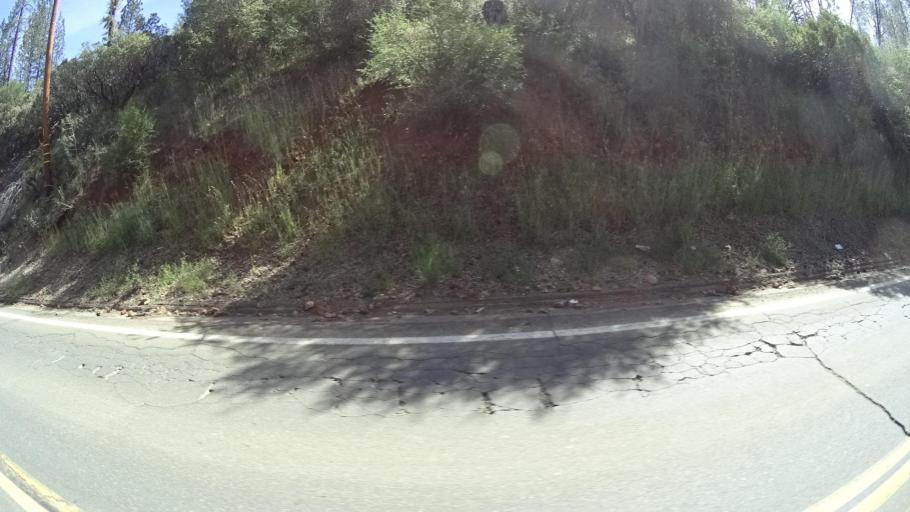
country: US
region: California
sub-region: Lake County
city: Cobb
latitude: 38.8536
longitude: -122.7581
